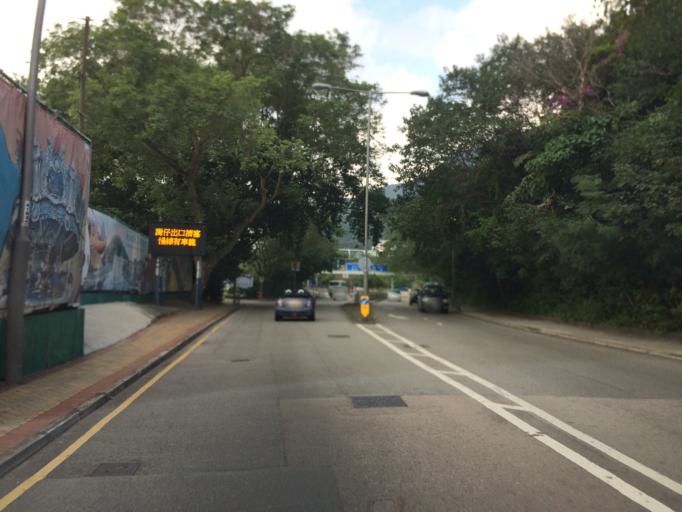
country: HK
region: Wanchai
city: Wan Chai
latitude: 22.2468
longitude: 114.1773
